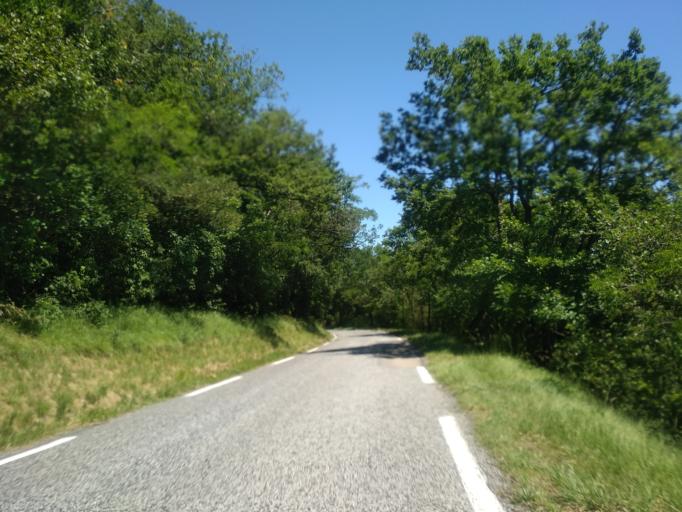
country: FR
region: Rhone-Alpes
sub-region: Departement du Rhone
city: Albigny-sur-Saone
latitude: 45.8507
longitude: 4.8153
